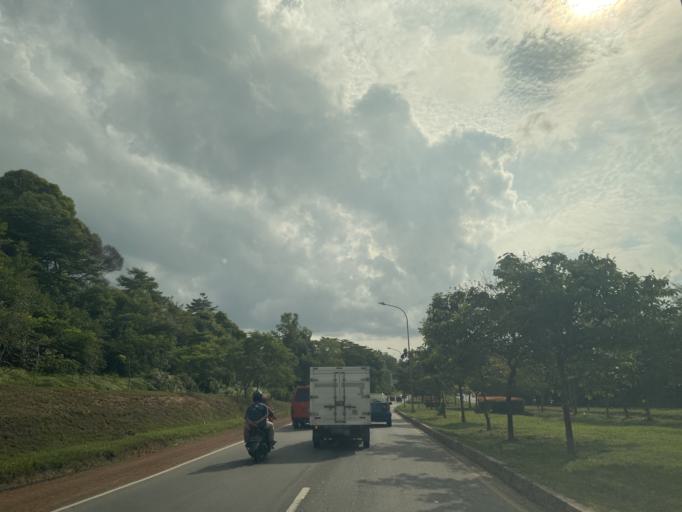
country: SG
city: Singapore
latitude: 1.0989
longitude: 104.0663
